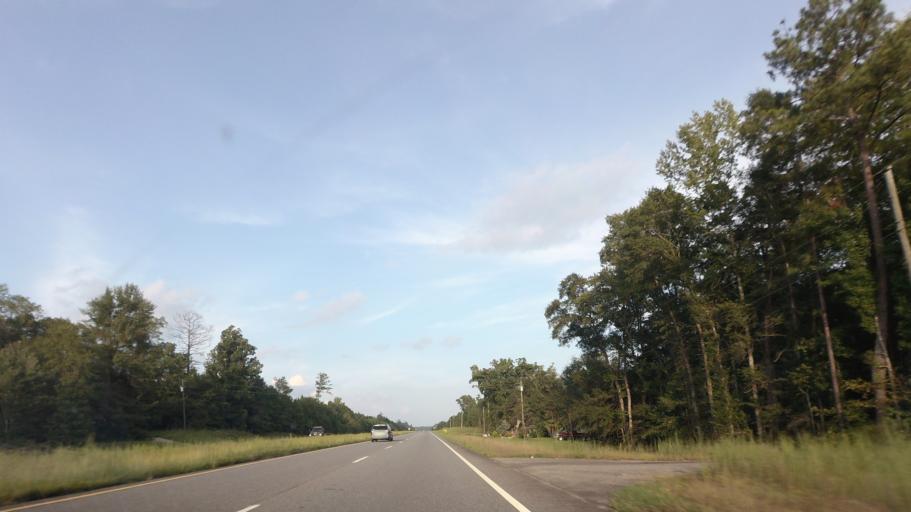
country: US
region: Georgia
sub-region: Wilkinson County
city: Gordon
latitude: 32.8500
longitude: -83.4123
